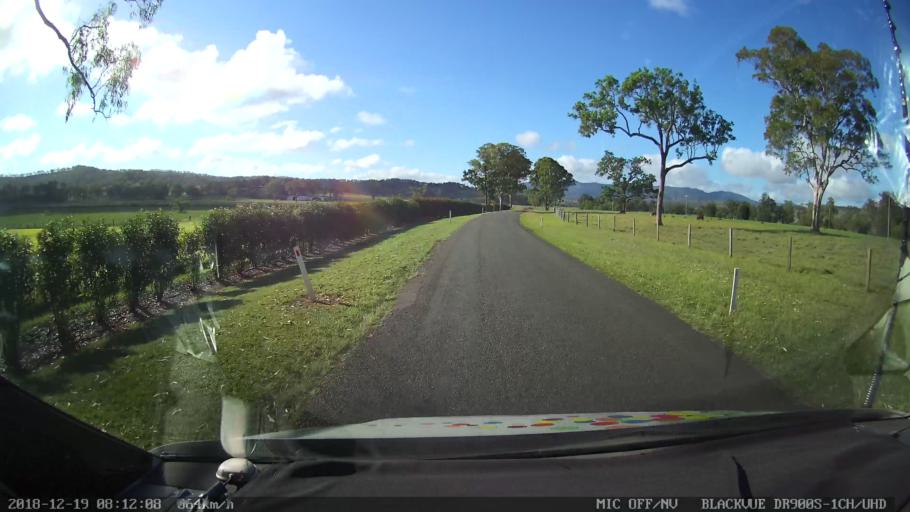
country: AU
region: Queensland
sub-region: Logan
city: Cedar Vale
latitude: -28.2246
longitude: 152.8920
